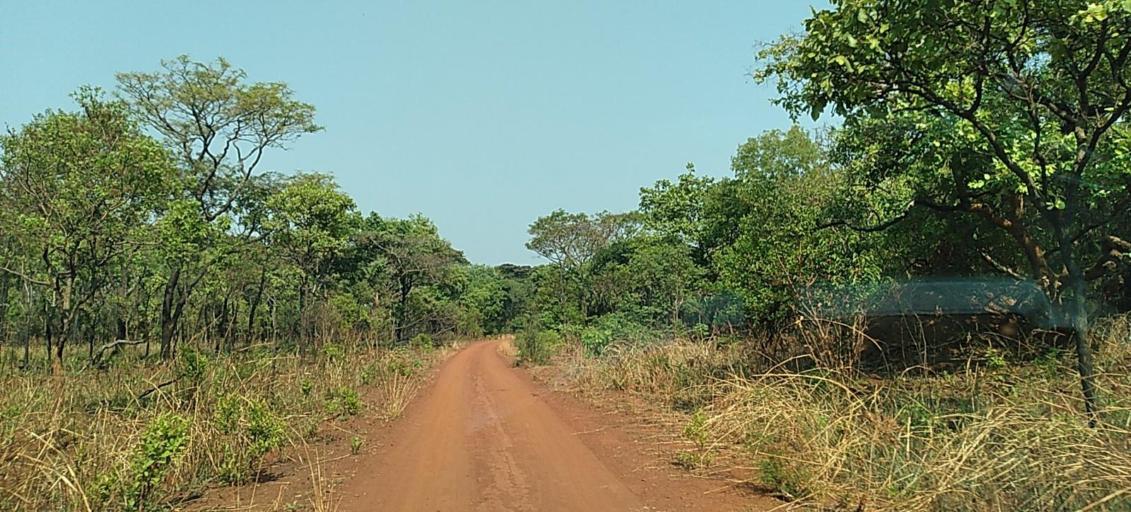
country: ZM
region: Copperbelt
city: Chingola
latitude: -12.8855
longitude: 27.4150
